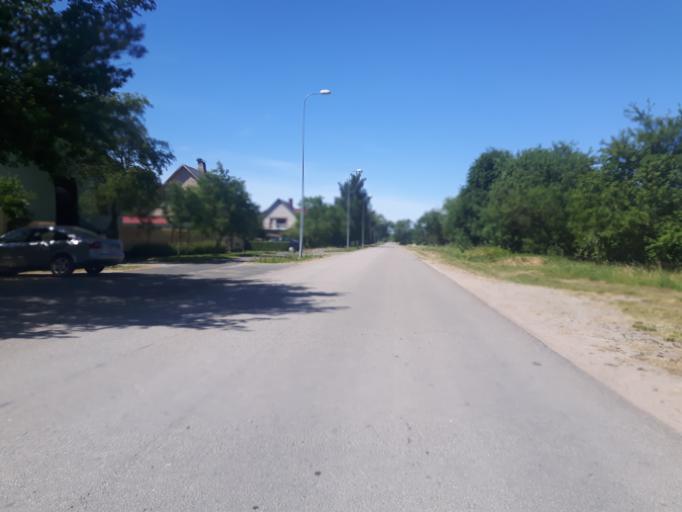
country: LV
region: Grobina
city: Grobina
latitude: 56.5382
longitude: 21.1634
